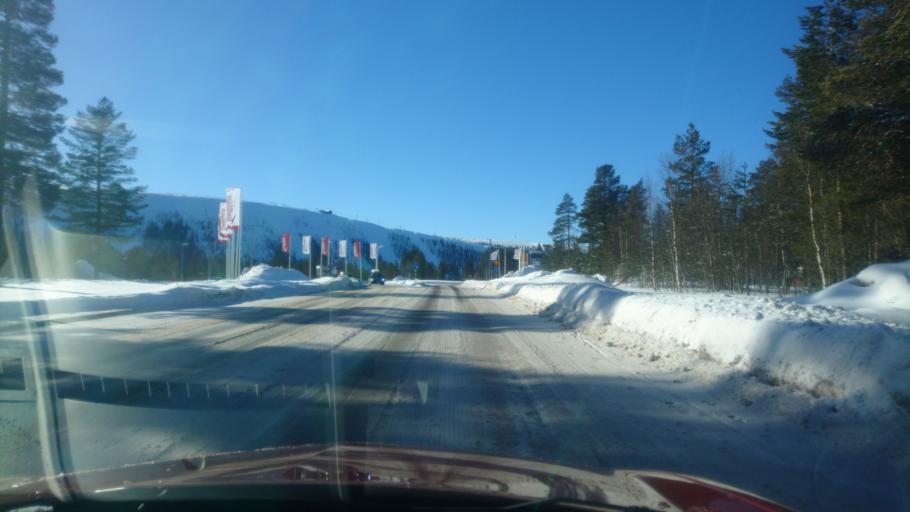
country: NO
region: Hedmark
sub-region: Trysil
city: Innbygda
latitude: 61.1803
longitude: 12.9934
